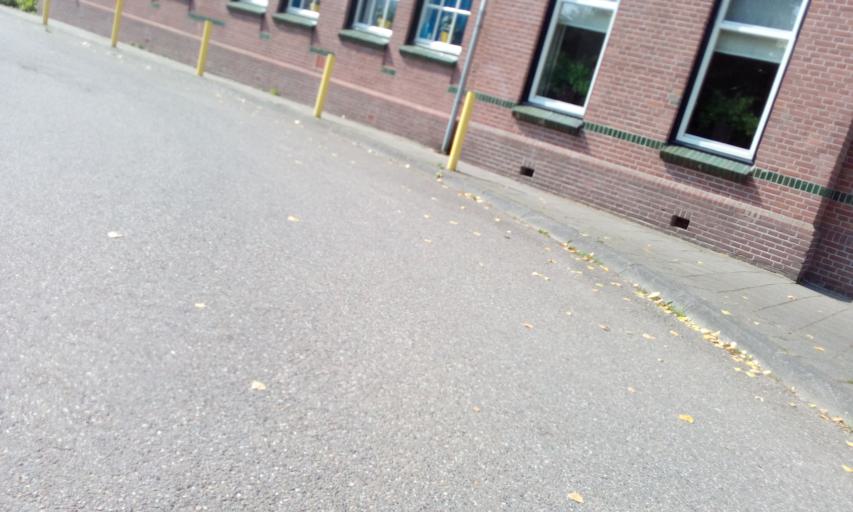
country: NL
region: South Holland
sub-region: Gemeente Capelle aan den IJssel
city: Capelle aan den IJssel
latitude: 51.9714
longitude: 4.5592
